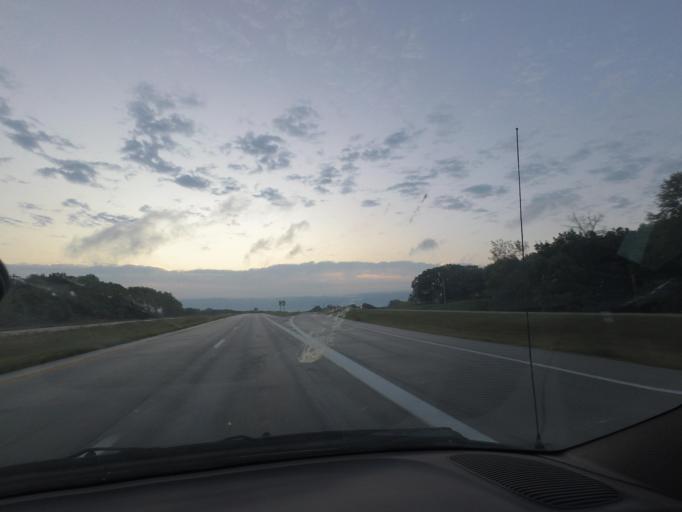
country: US
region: Missouri
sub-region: Macon County
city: Macon
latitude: 39.7487
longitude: -92.5095
